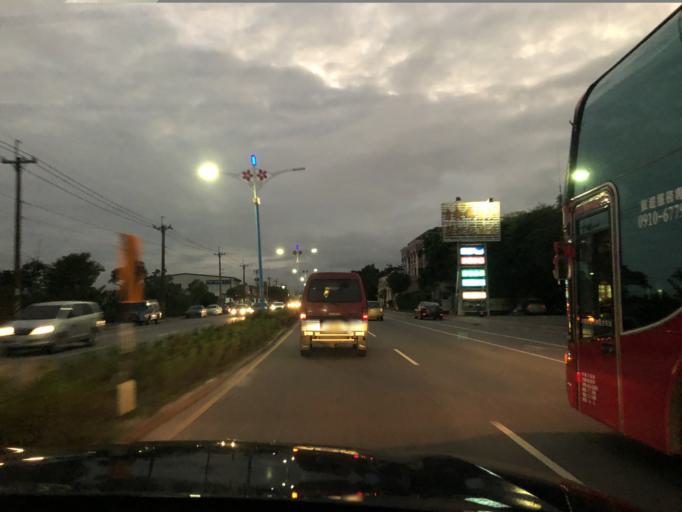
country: TW
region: Taiwan
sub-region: Hualien
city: Hualian
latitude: 23.9743
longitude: 121.5734
